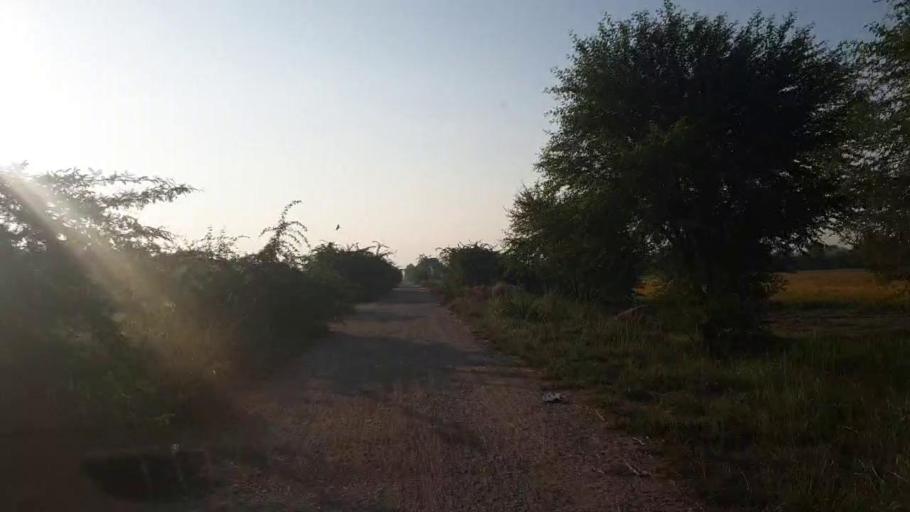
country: PK
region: Sindh
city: Badin
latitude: 24.6581
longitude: 68.7874
